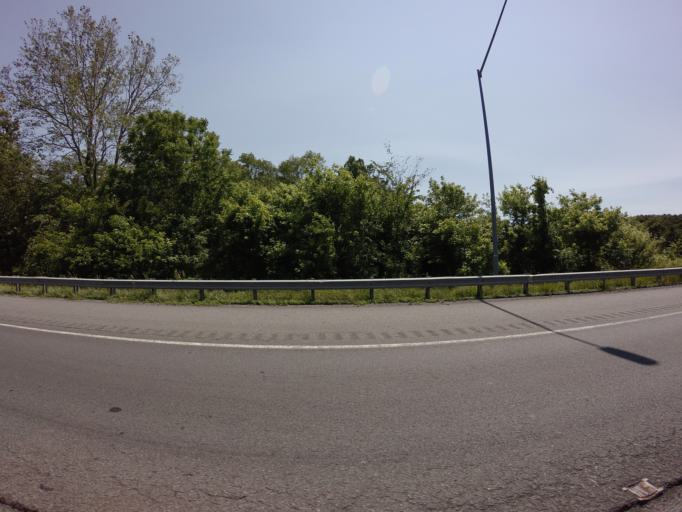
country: US
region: Maryland
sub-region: Frederick County
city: Linganore
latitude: 39.3785
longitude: -77.2461
